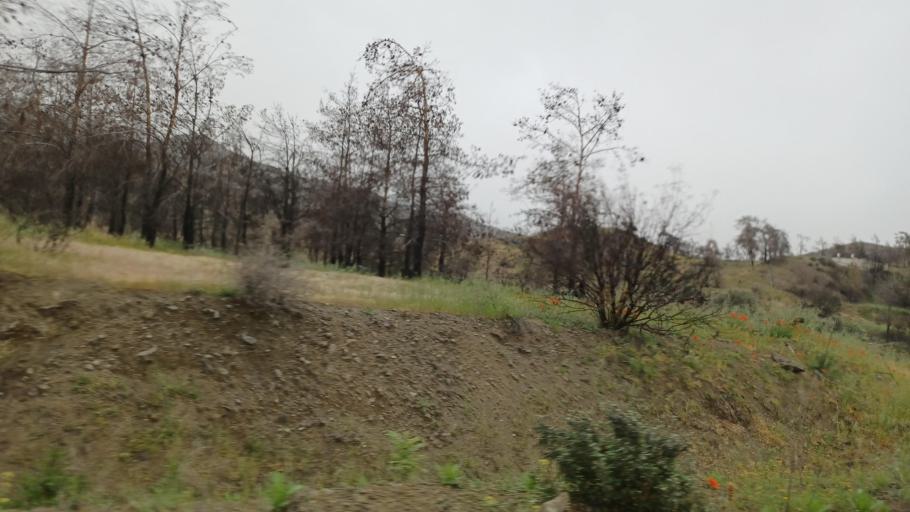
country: CY
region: Limassol
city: Parekklisha
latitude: 34.8398
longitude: 33.1300
